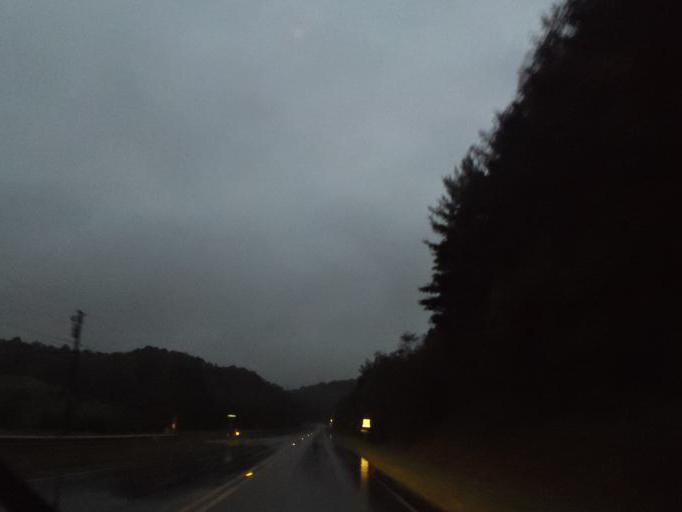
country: US
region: North Carolina
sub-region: Alleghany County
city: Sparta
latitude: 36.5418
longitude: -81.1557
